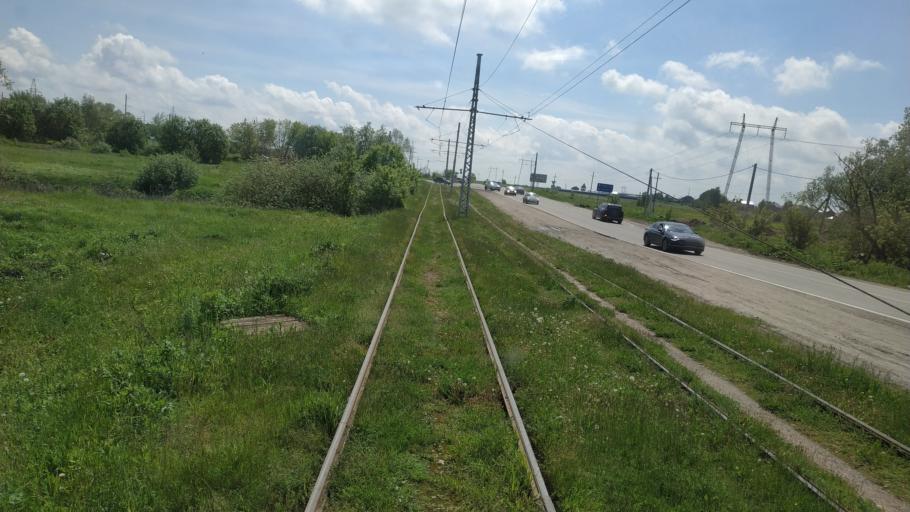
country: RU
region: Moskovskaya
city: Sychevo
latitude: 55.0609
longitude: 38.7266
